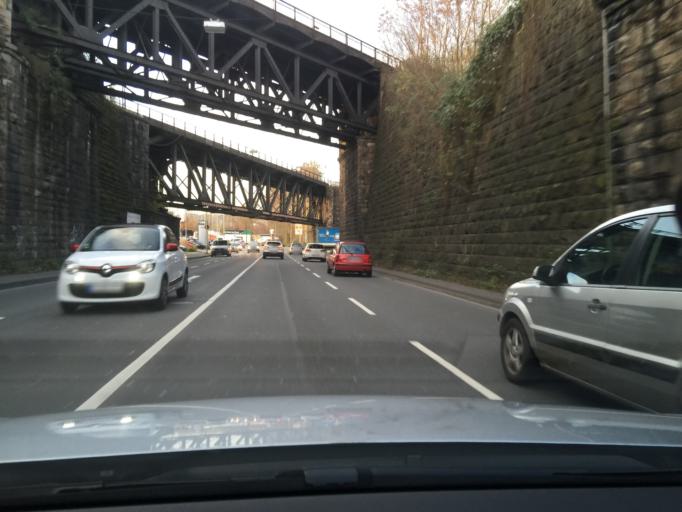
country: DE
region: North Rhine-Westphalia
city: Herdecke
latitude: 51.3865
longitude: 7.4460
